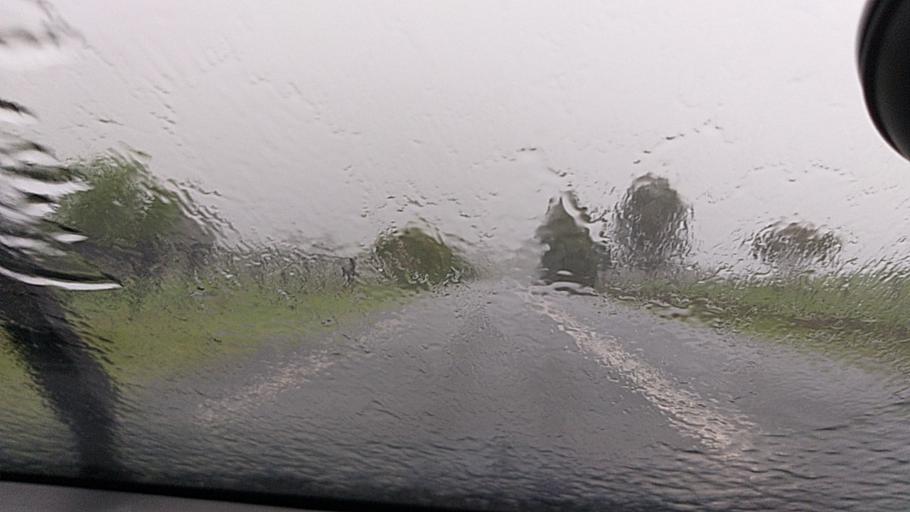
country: AU
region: New South Wales
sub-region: Wollondilly
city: Douglas Park
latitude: -34.1422
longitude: 150.7162
